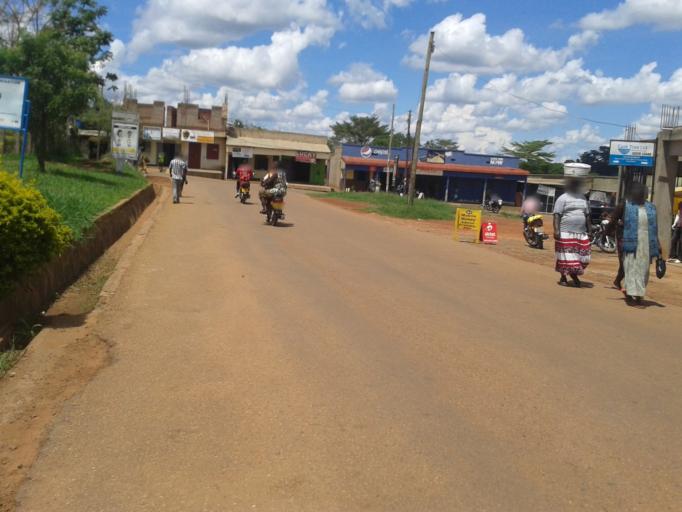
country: UG
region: Northern Region
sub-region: Gulu District
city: Gulu
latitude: 2.7765
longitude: 32.2989
